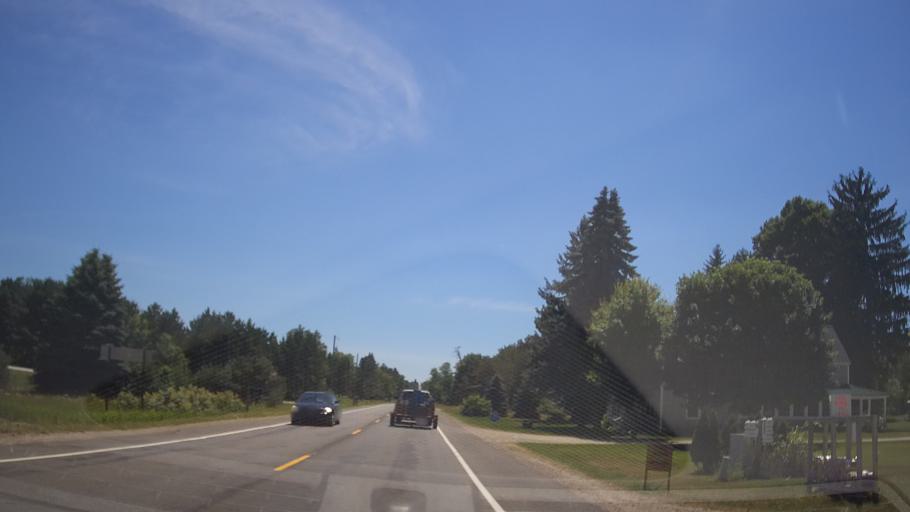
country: US
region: Michigan
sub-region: Grand Traverse County
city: Traverse City
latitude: 44.6422
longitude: -85.6964
